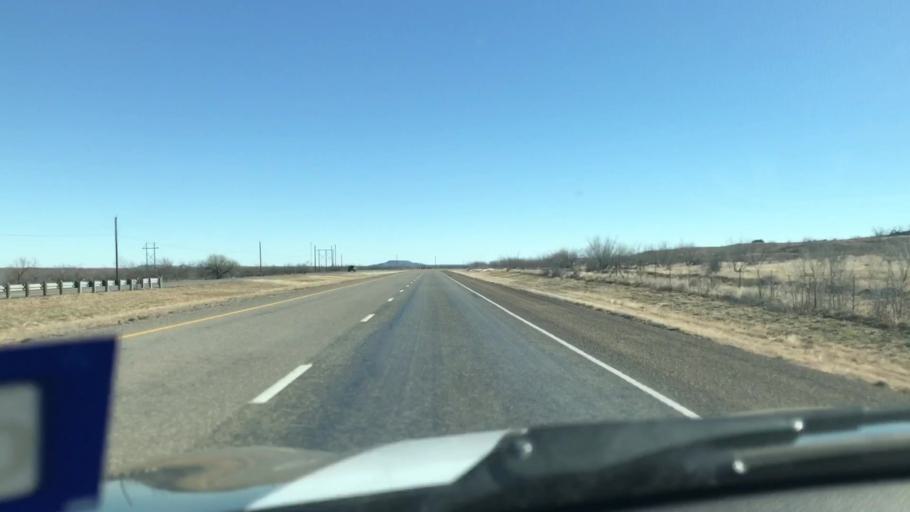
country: US
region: Texas
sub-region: Garza County
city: Post
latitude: 33.0633
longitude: -101.2214
